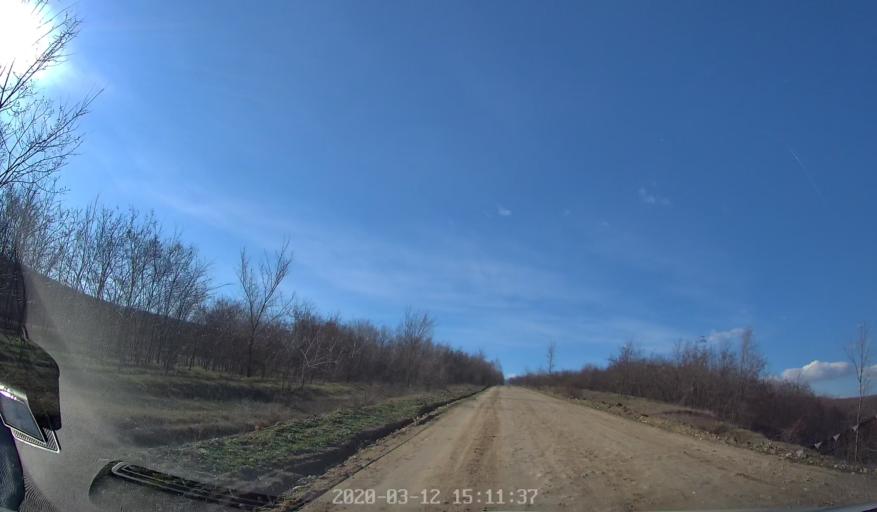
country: MD
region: Chisinau
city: Ciorescu
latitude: 47.2272
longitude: 28.9749
